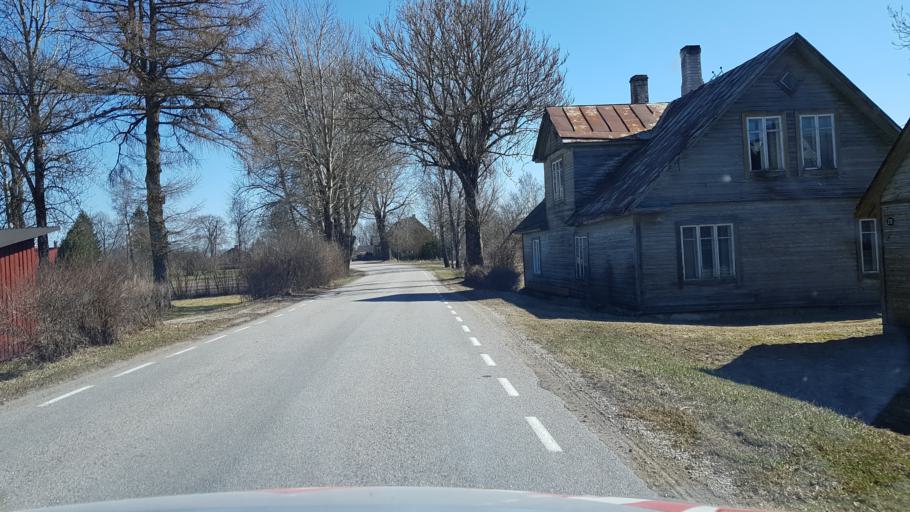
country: EE
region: Laeaene-Virumaa
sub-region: Vaeike-Maarja vald
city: Vaike-Maarja
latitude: 59.1149
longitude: 26.3650
